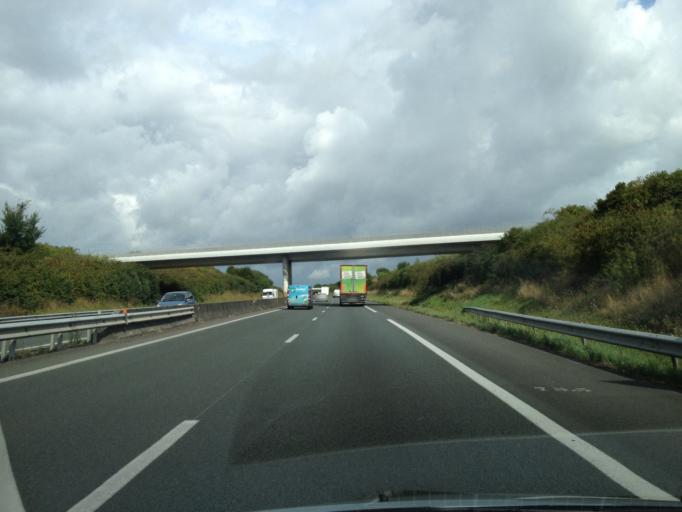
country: FR
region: Pays de la Loire
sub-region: Departement de la Vendee
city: Sainte-Hermine
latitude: 46.5472
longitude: -1.0876
